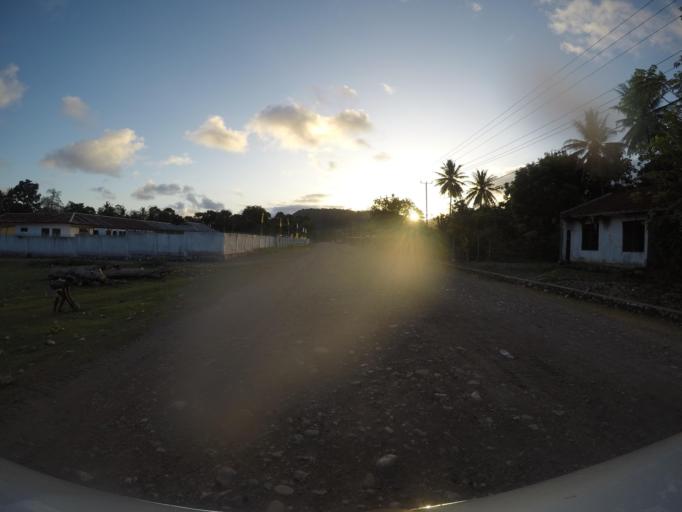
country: TL
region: Baucau
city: Venilale
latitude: -8.7497
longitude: 126.6991
